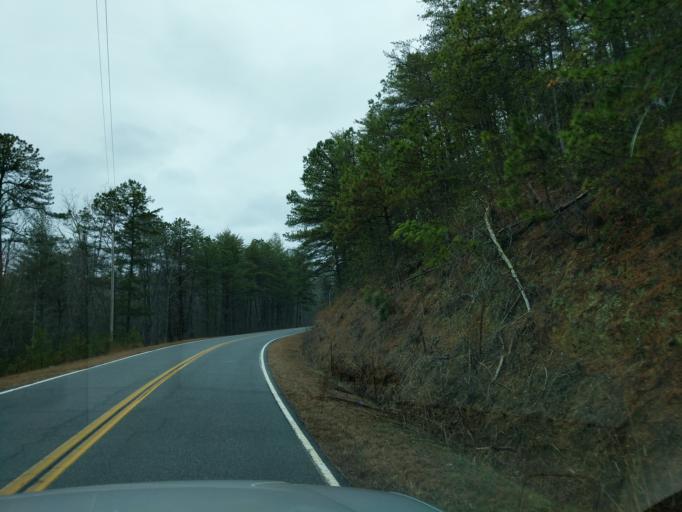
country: US
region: South Carolina
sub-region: Oconee County
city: Walhalla
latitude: 34.7915
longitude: -83.2183
